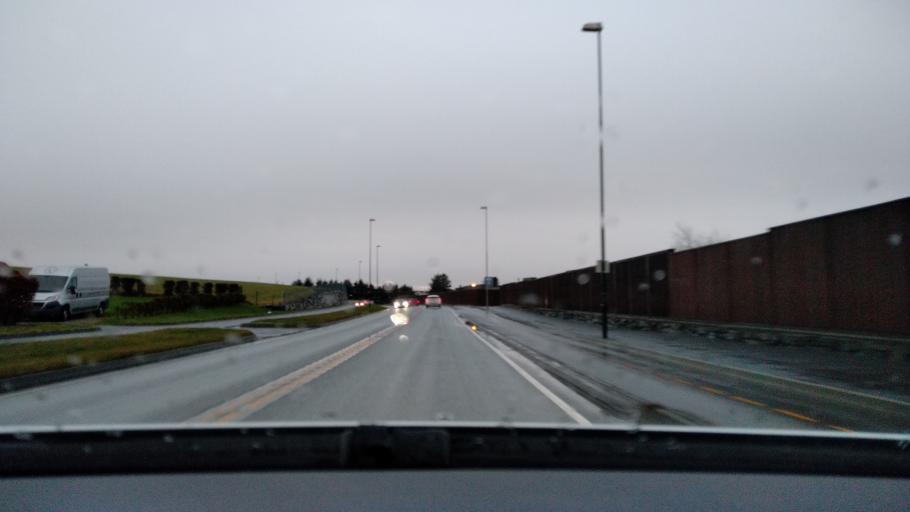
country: NO
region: Rogaland
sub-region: Randaberg
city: Randaberg
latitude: 58.9555
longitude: 5.6375
